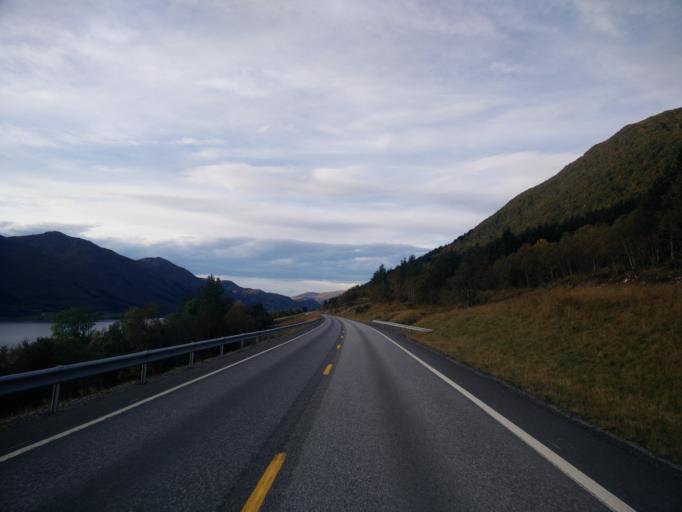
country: NO
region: More og Romsdal
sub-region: Gjemnes
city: Batnfjordsora
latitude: 62.9429
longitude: 7.7426
